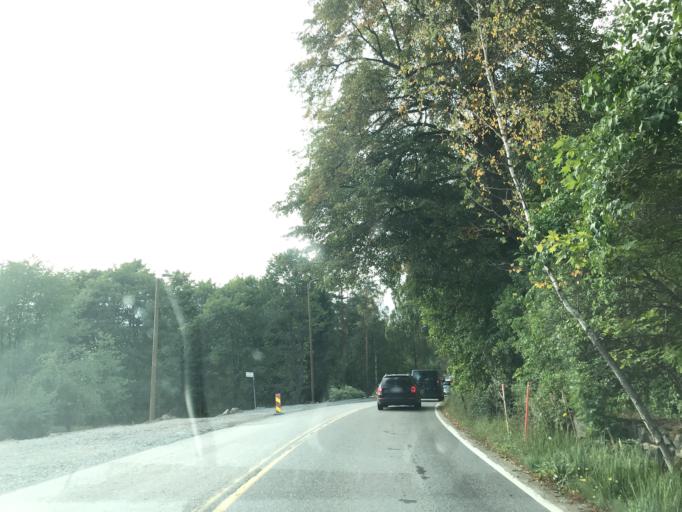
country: FI
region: Uusimaa
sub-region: Helsinki
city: Kirkkonummi
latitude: 60.2163
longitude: 24.4787
